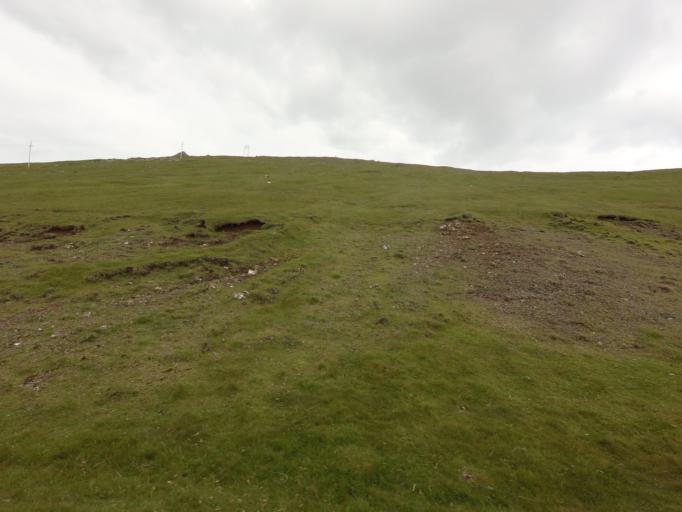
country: FO
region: Suduroy
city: Vagur
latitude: 61.4256
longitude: -6.7539
